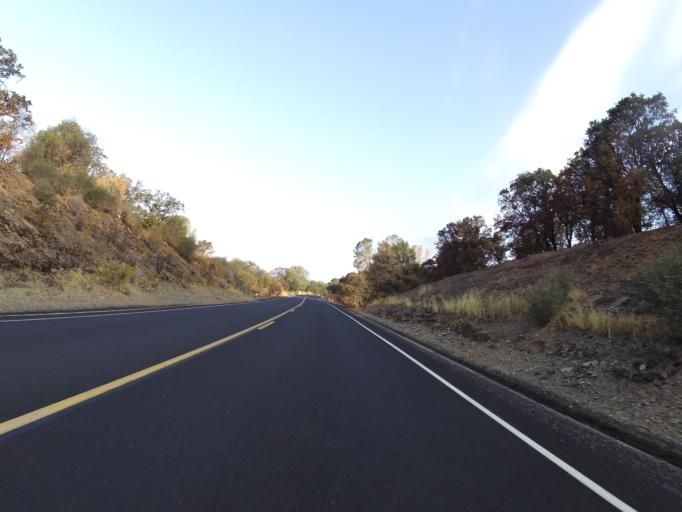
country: US
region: California
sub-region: Mariposa County
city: Mariposa
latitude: 37.5401
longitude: -120.0917
